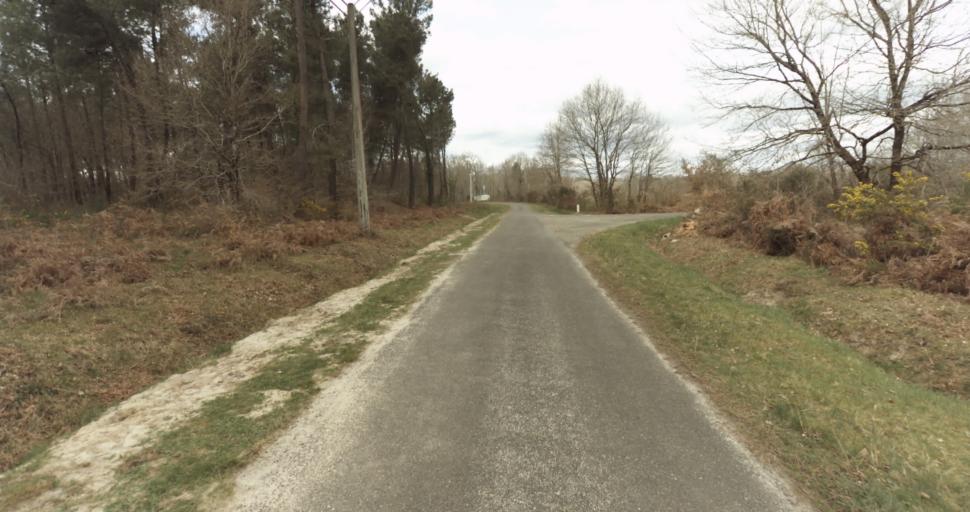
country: FR
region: Aquitaine
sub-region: Departement des Landes
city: Roquefort
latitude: 44.0755
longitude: -0.3978
